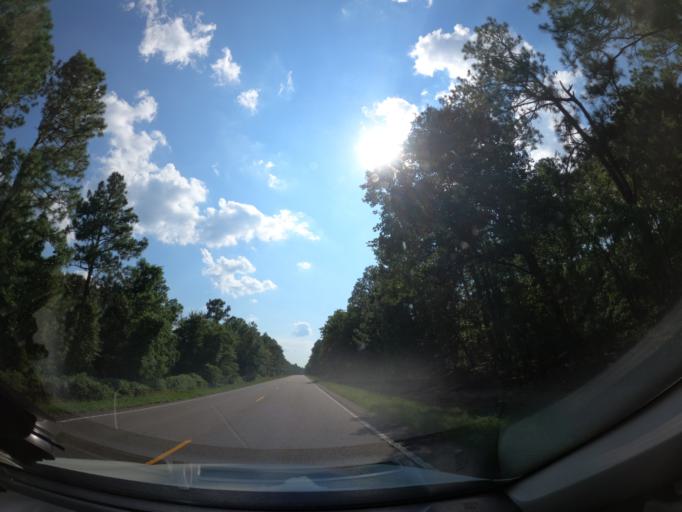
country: US
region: South Carolina
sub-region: Aiken County
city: New Ellenton
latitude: 33.3936
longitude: -81.5603
